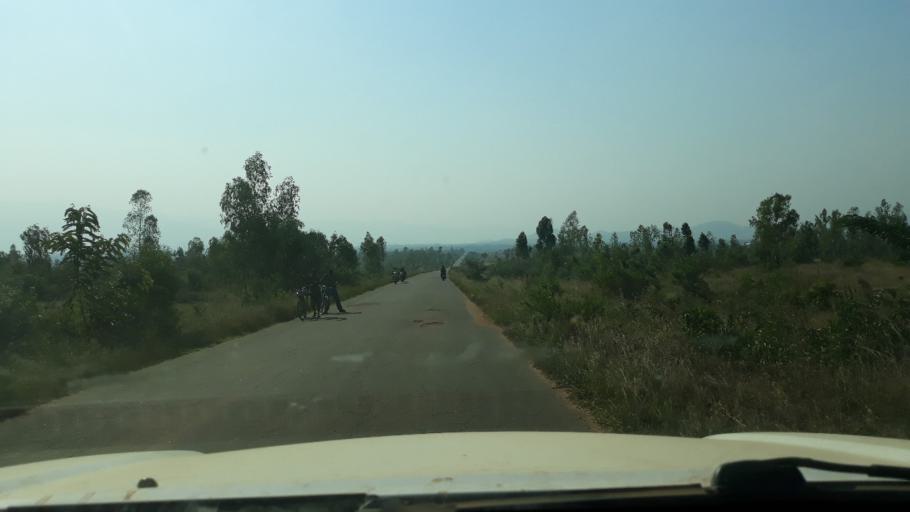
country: BI
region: Cibitoke
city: Cibitoke
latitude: -2.8926
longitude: 29.0477
